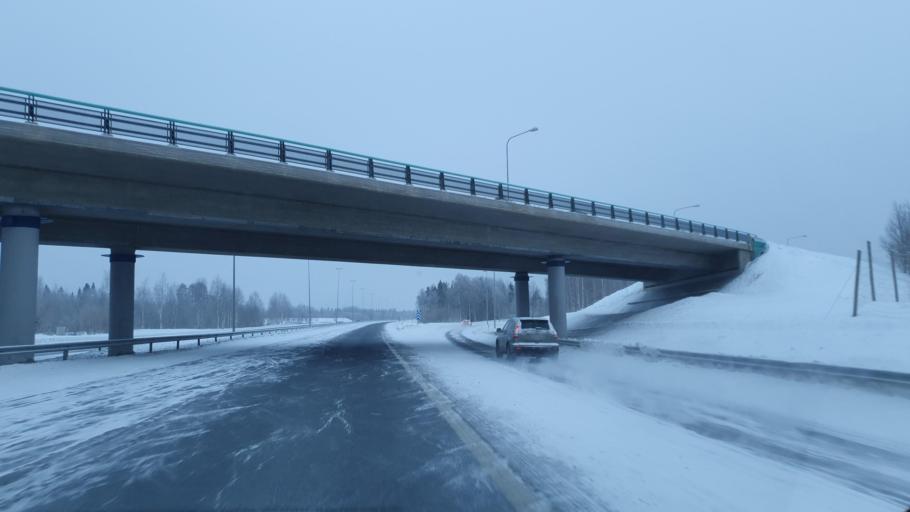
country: FI
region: Lapland
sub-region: Kemi-Tornio
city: Tornio
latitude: 65.8379
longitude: 24.2789
